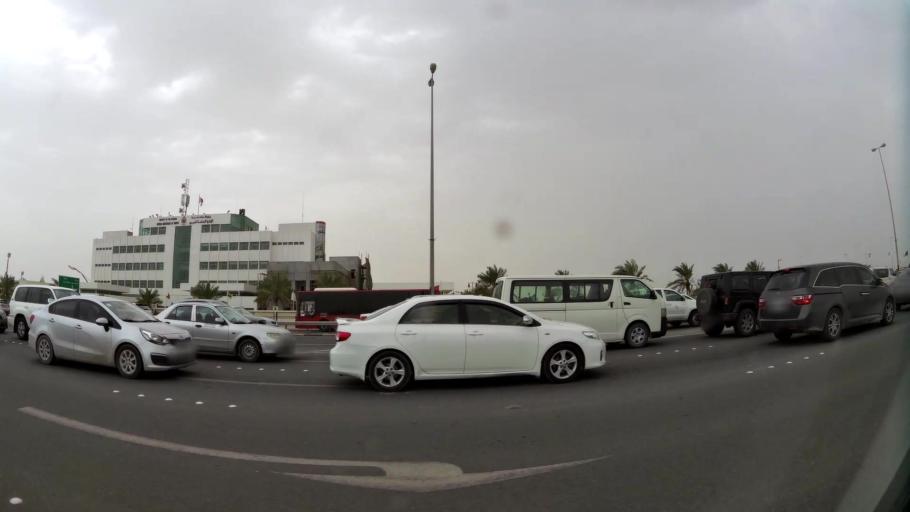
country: BH
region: Northern
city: Madinat `Isa
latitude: 26.1575
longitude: 50.5379
